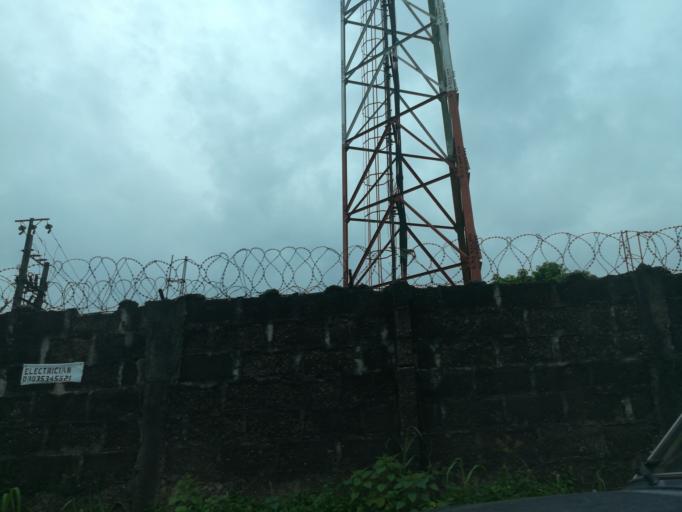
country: NG
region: Rivers
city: Port Harcourt
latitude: 4.8197
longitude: 7.0174
